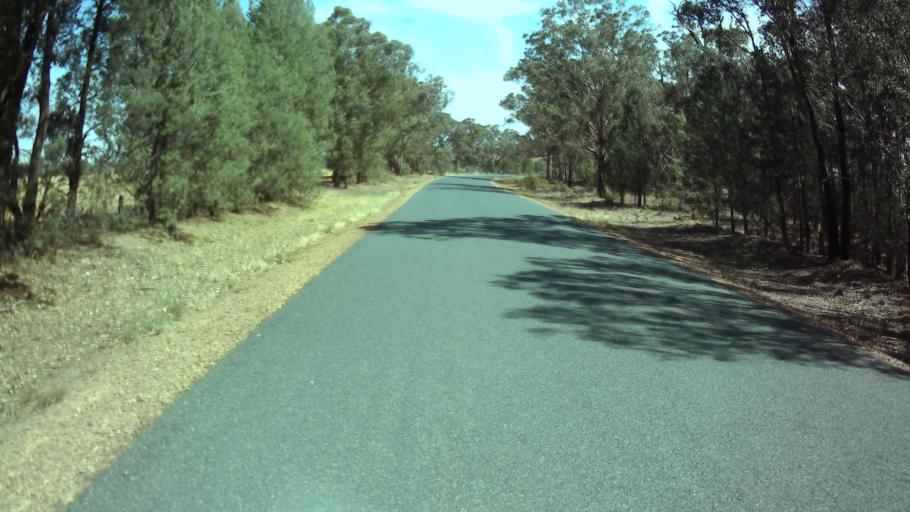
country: AU
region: New South Wales
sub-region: Weddin
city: Grenfell
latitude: -34.0358
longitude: 148.1344
